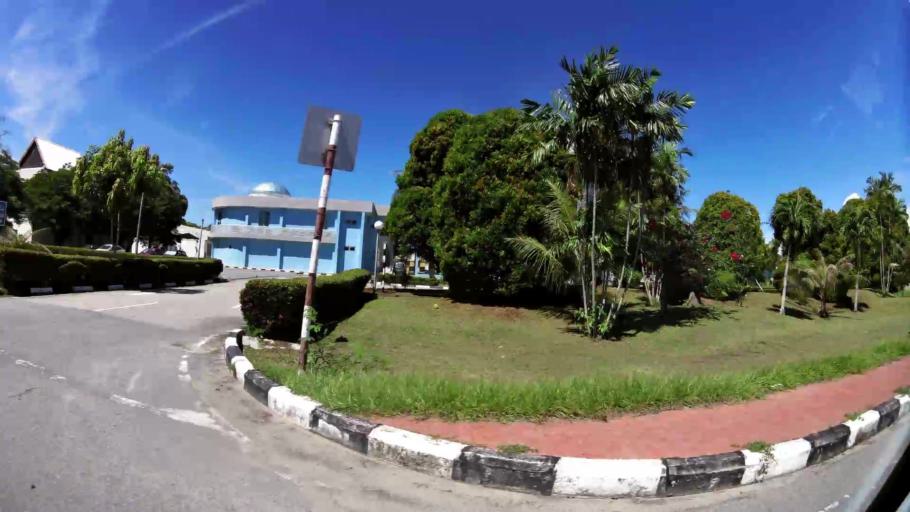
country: BN
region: Brunei and Muara
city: Bandar Seri Begawan
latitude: 5.0294
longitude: 115.0712
